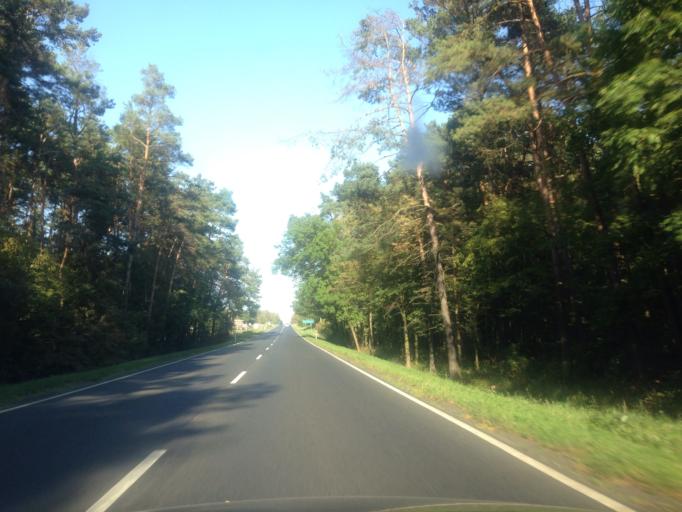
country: PL
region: Kujawsko-Pomorskie
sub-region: Powiat brodnicki
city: Brzozie
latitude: 53.3142
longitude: 19.5232
